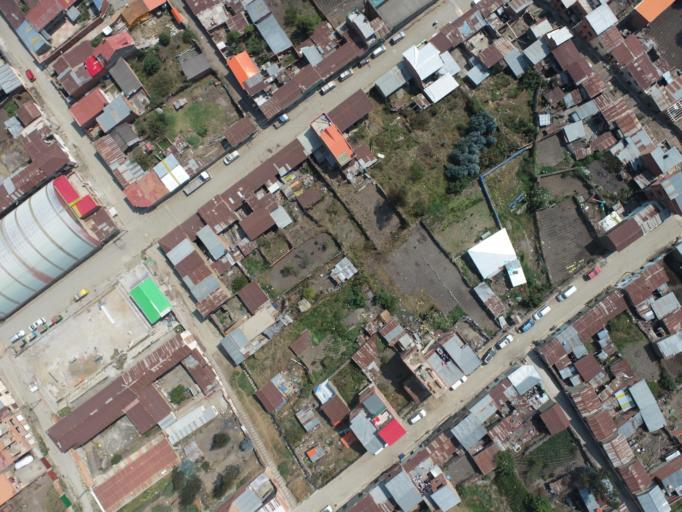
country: BO
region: La Paz
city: Quime
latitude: -16.9818
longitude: -67.2174
